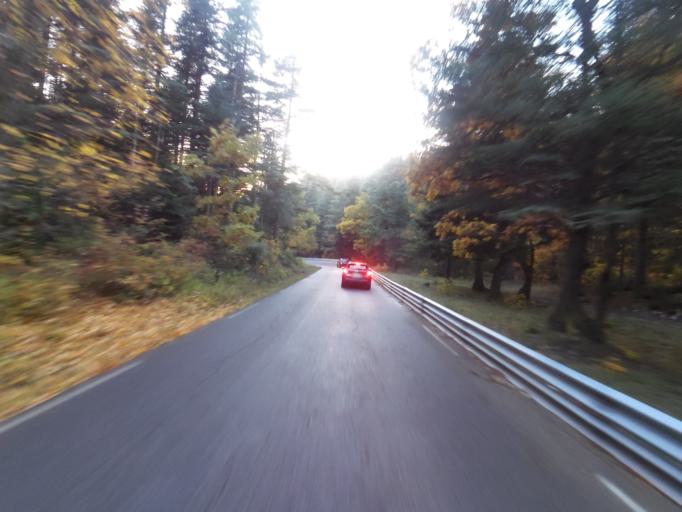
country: FR
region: Provence-Alpes-Cote d'Azur
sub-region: Departement du Vaucluse
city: Villes-sur-Auzon
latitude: 44.1247
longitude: 5.2545
